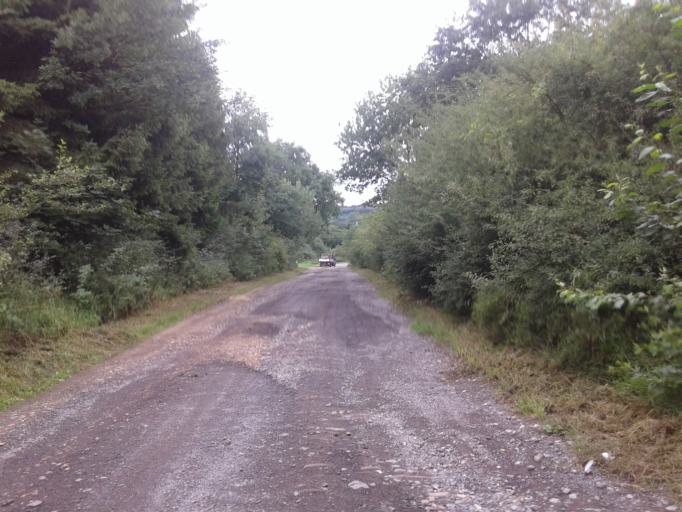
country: BE
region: Wallonia
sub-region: Province du Luxembourg
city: Tintigny
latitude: 49.7326
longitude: 5.5401
